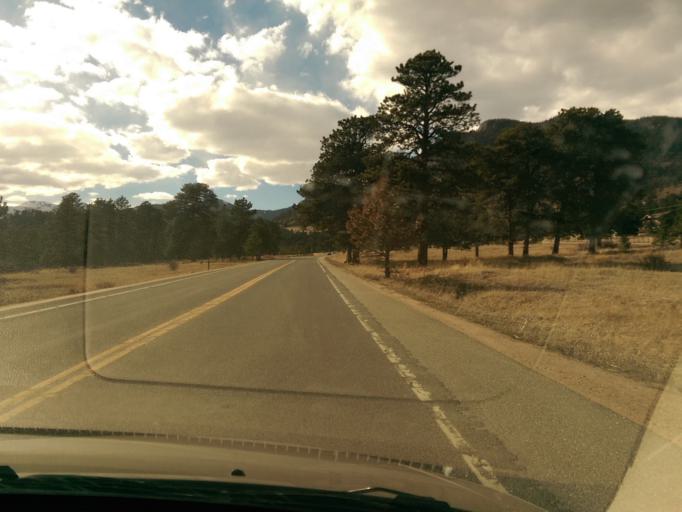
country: US
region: Colorado
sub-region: Larimer County
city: Estes Park
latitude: 40.3657
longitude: -105.5565
